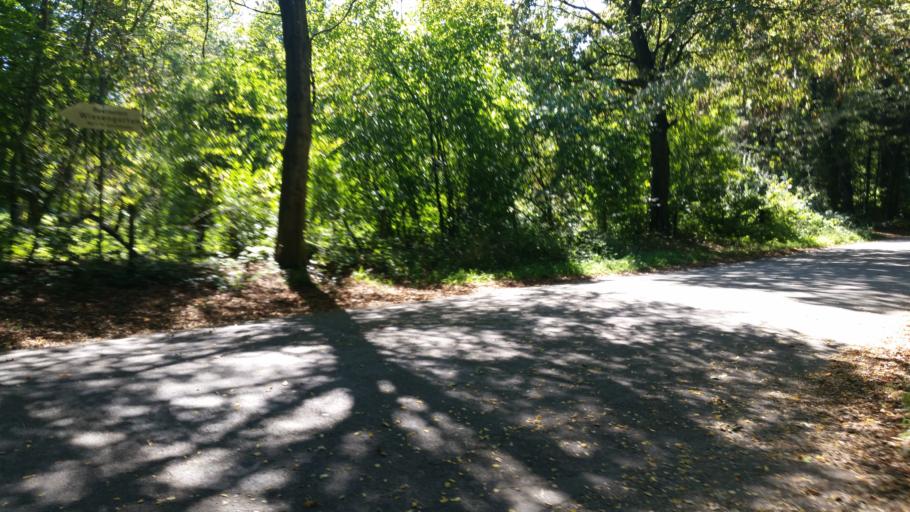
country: DE
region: Baden-Wuerttemberg
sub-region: Freiburg Region
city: Weil am Rhein
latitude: 47.5804
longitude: 7.6298
